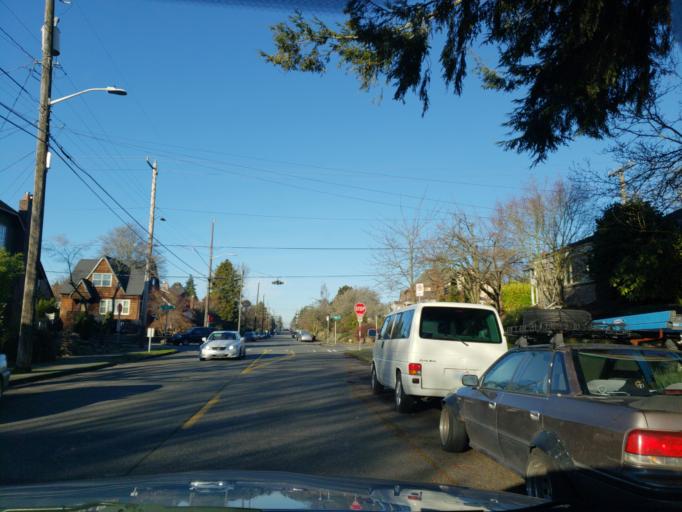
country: US
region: Washington
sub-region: King County
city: Lake Forest Park
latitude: 47.6863
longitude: -122.3068
